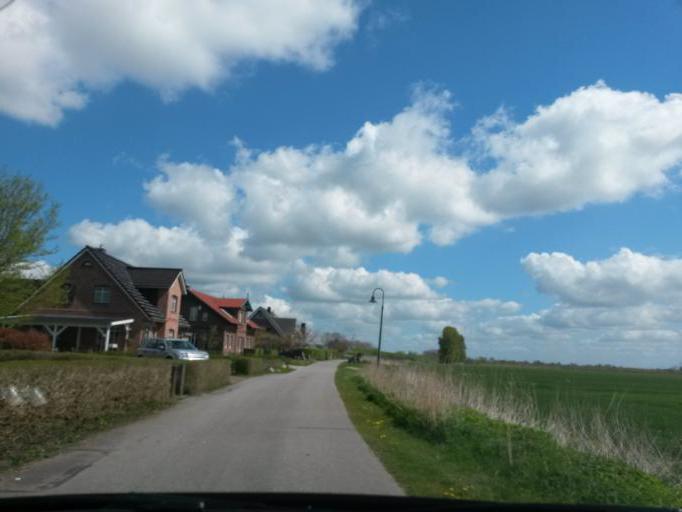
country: DE
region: Schleswig-Holstein
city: Seestermuhe
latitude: 53.6675
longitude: 9.5760
